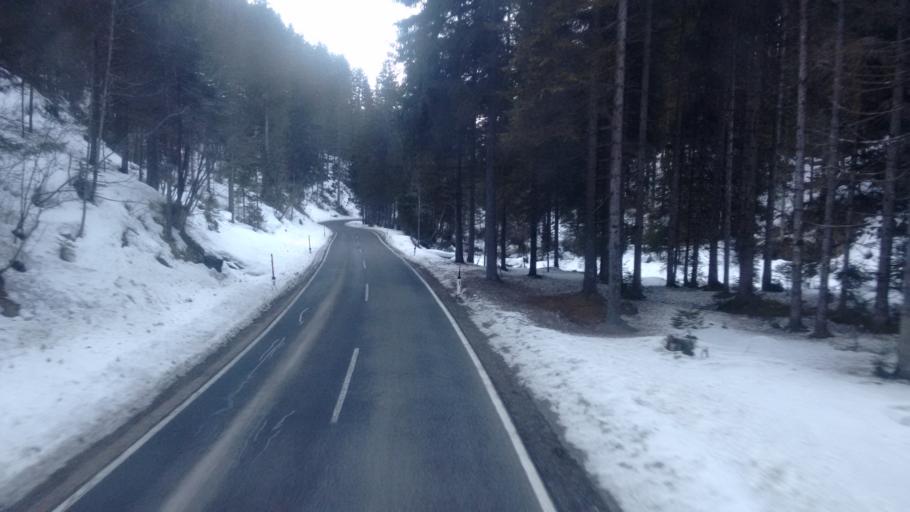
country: AT
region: Salzburg
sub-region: Politischer Bezirk Sankt Johann im Pongau
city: Radstadt
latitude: 47.3417
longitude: 13.4357
